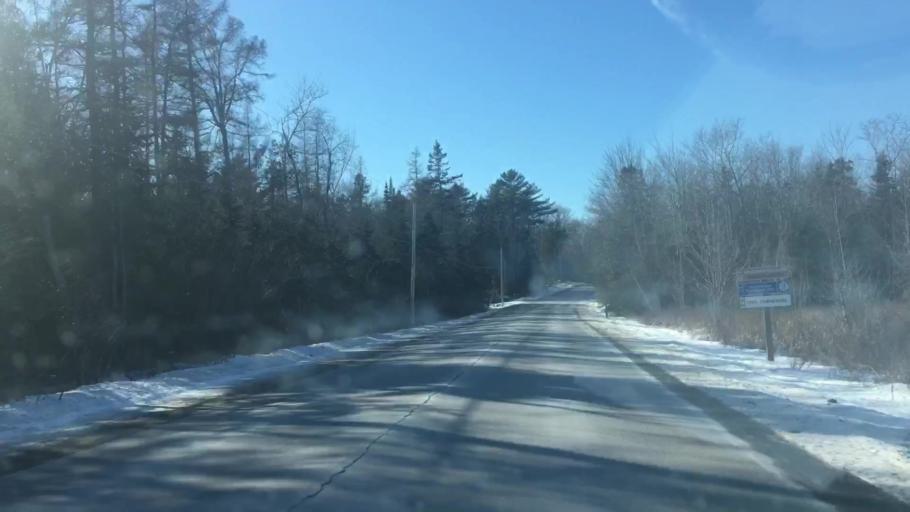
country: US
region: Maine
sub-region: Hancock County
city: Sedgwick
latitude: 44.3808
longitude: -68.6551
